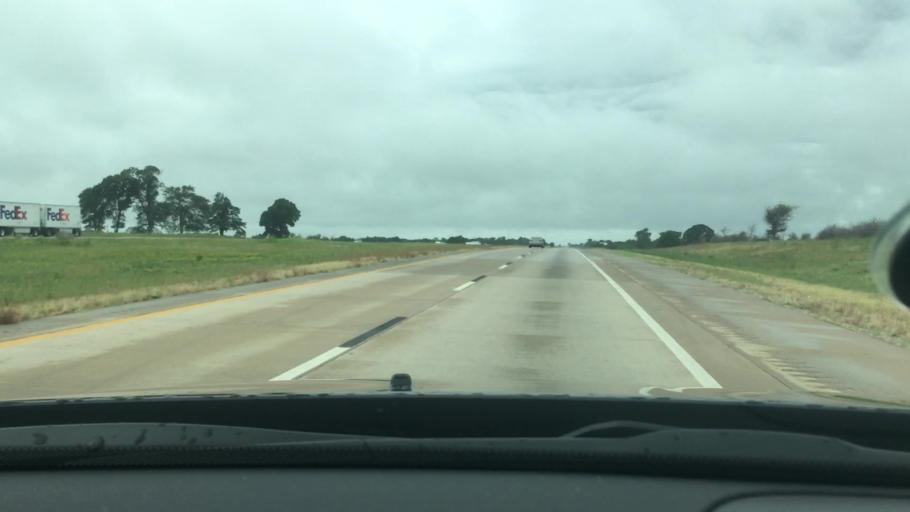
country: US
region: Oklahoma
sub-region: Atoka County
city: Atoka
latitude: 34.2249
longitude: -96.2268
